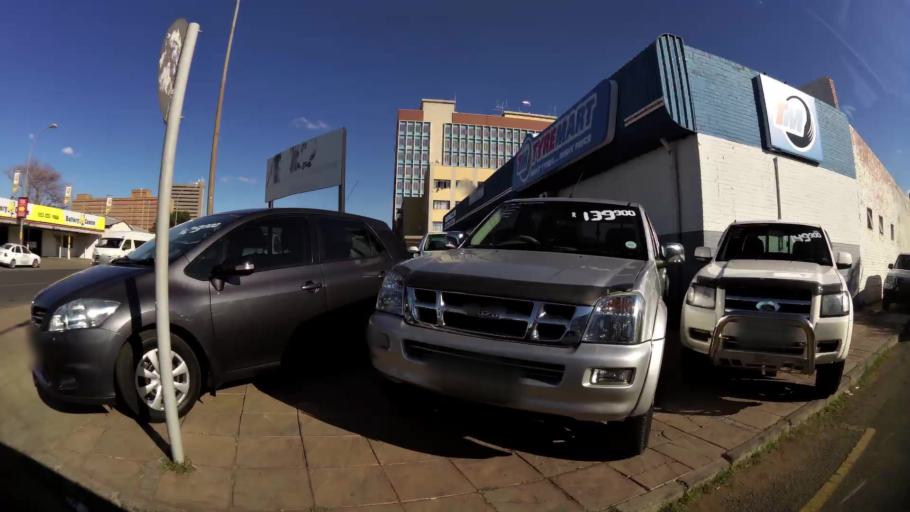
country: ZA
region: Northern Cape
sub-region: Frances Baard District Municipality
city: Kimberley
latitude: -28.7339
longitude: 24.7636
